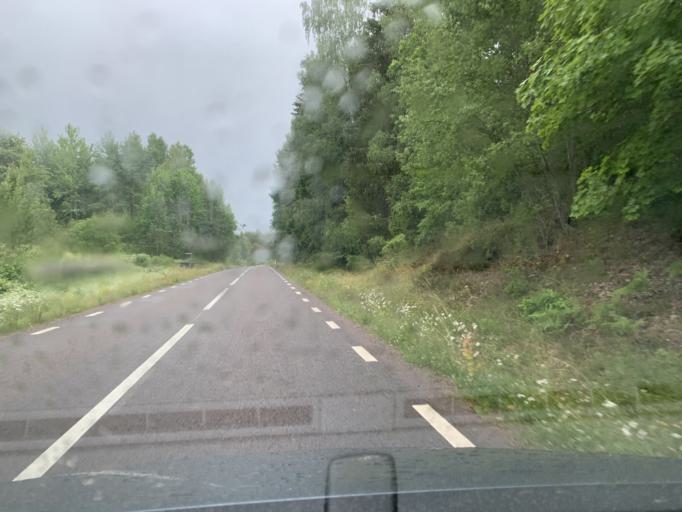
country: SE
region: Kalmar
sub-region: Vasterviks Kommun
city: Overum
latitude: 58.0059
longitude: 16.1733
